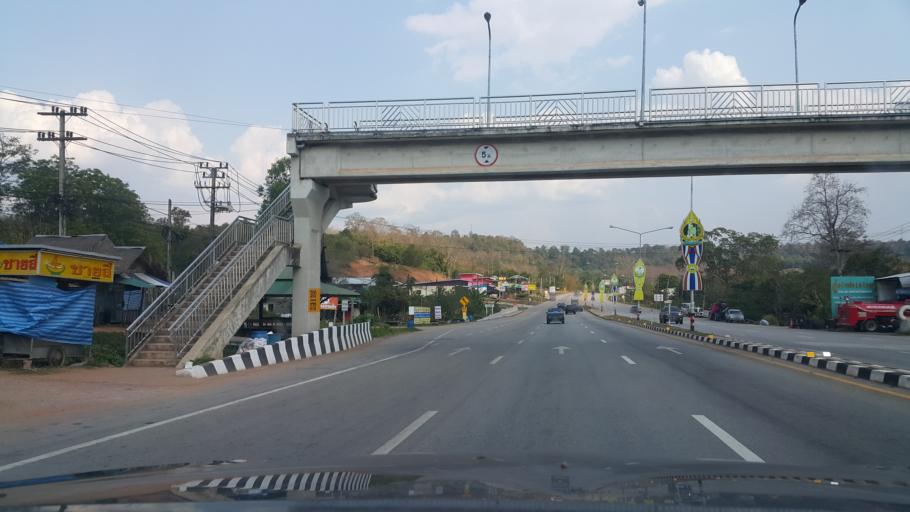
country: TH
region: Phitsanulok
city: Nakhon Thai
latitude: 16.8885
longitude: 100.8023
